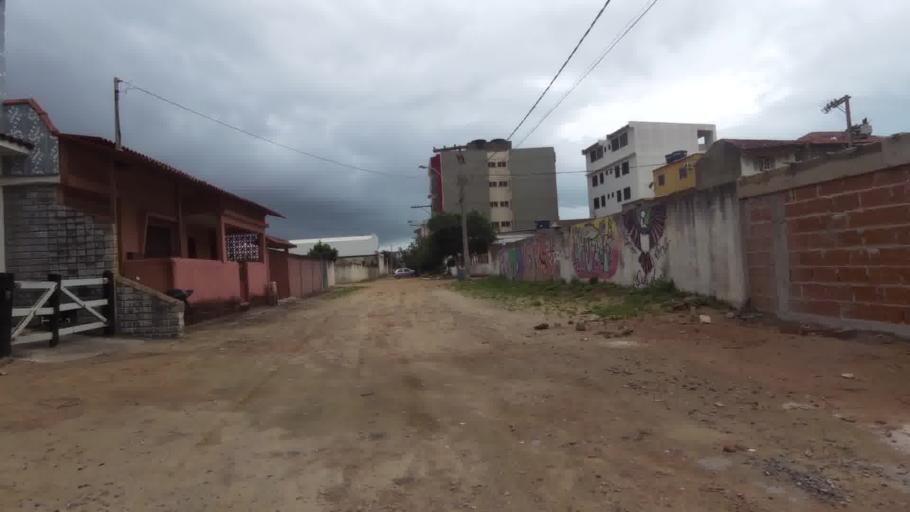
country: BR
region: Espirito Santo
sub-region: Marataizes
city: Marataizes
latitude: -21.0521
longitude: -40.8324
